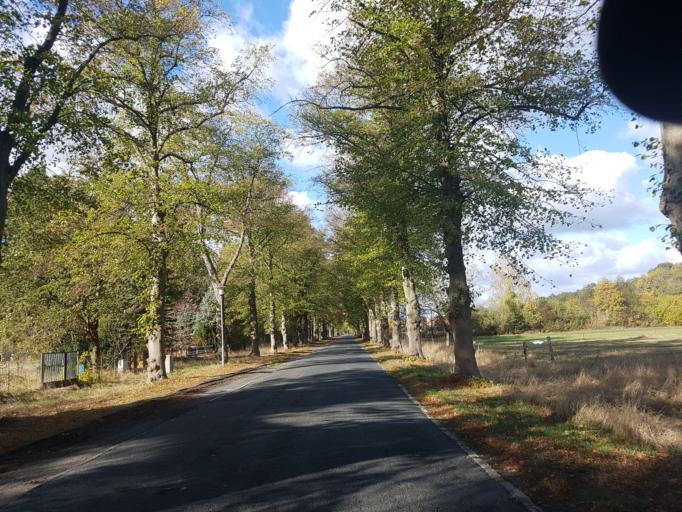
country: DE
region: Brandenburg
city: Nauen
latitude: 52.6602
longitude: 12.9183
